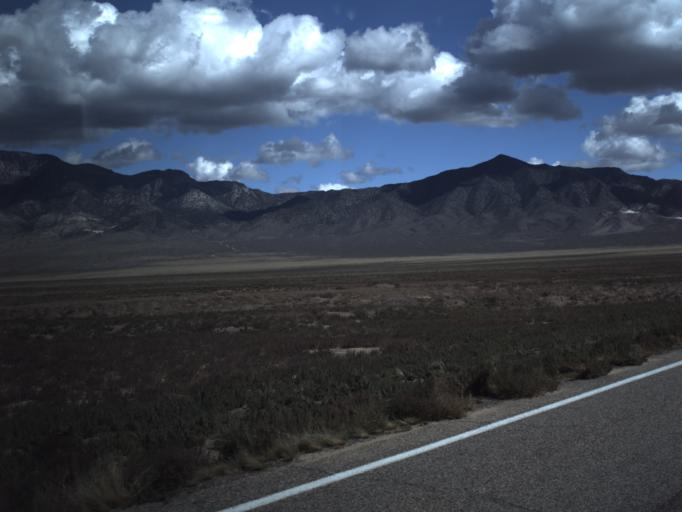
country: US
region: Utah
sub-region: Beaver County
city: Milford
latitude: 38.4638
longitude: -113.3864
